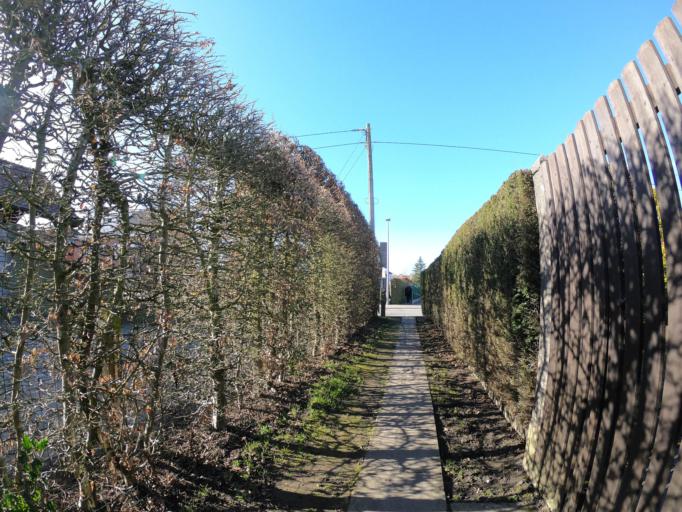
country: BE
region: Flanders
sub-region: Provincie West-Vlaanderen
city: Avelgem
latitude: 50.7790
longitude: 3.4520
